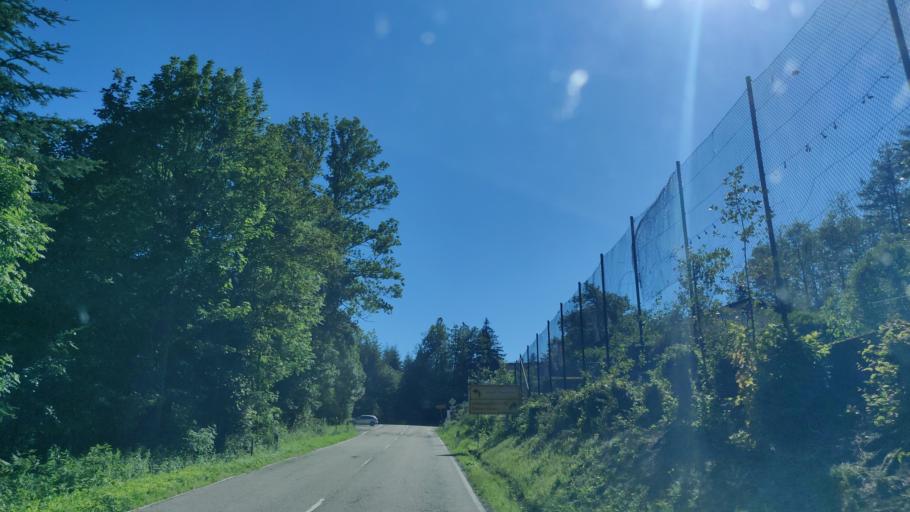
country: DE
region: Baden-Wuerttemberg
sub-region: Karlsruhe Region
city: Gernsbach
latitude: 48.7476
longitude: 8.3031
